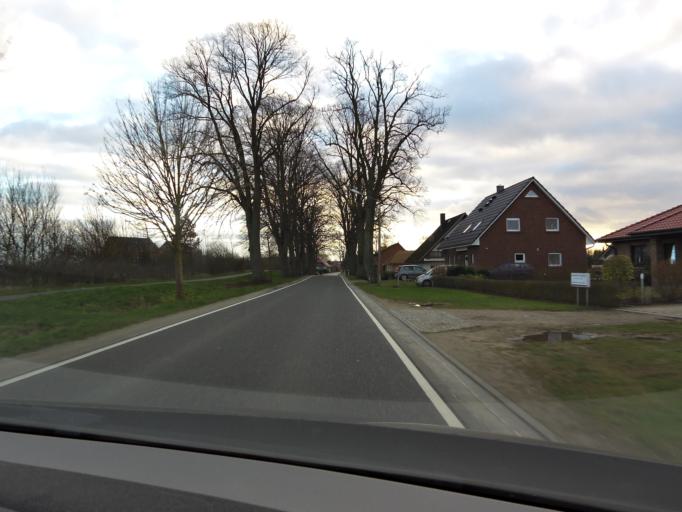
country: DE
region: Mecklenburg-Vorpommern
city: Zarrentin
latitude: 53.5603
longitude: 10.9086
